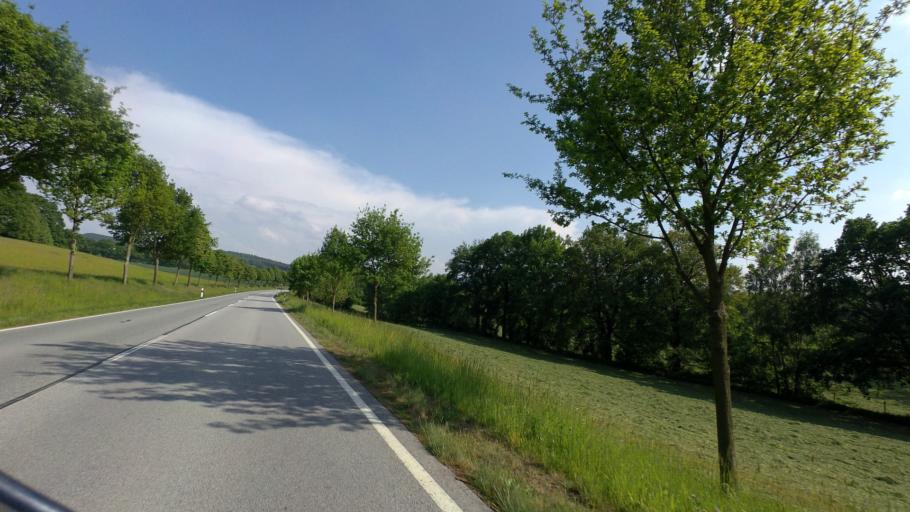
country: DE
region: Saxony
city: Grosspostwitz
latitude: 51.1165
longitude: 14.4486
